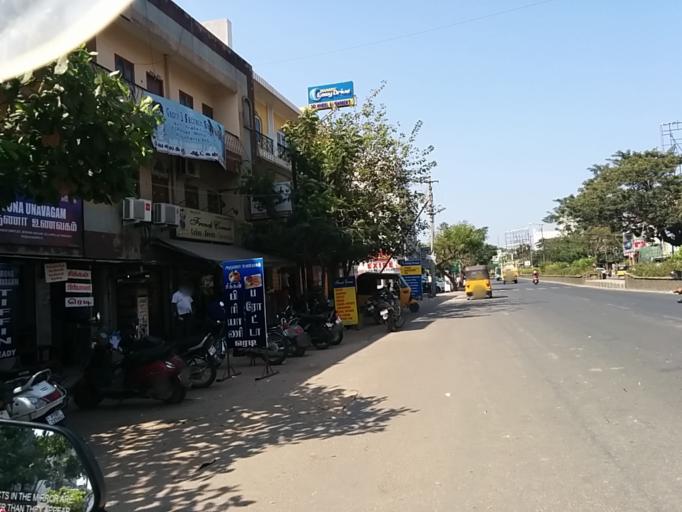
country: IN
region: Pondicherry
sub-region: Puducherry
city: Puducherry
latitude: 11.9391
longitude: 79.8080
